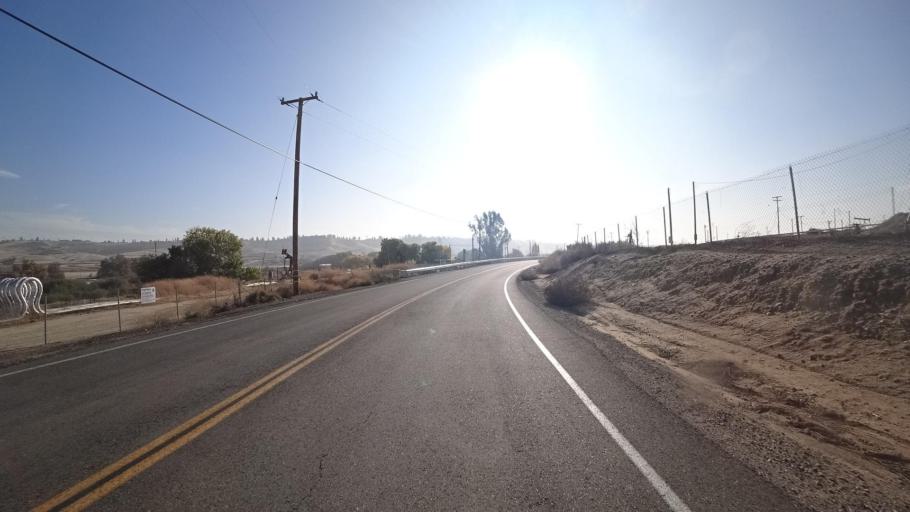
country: US
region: California
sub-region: Kern County
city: Oildale
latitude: 35.4286
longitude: -118.9543
